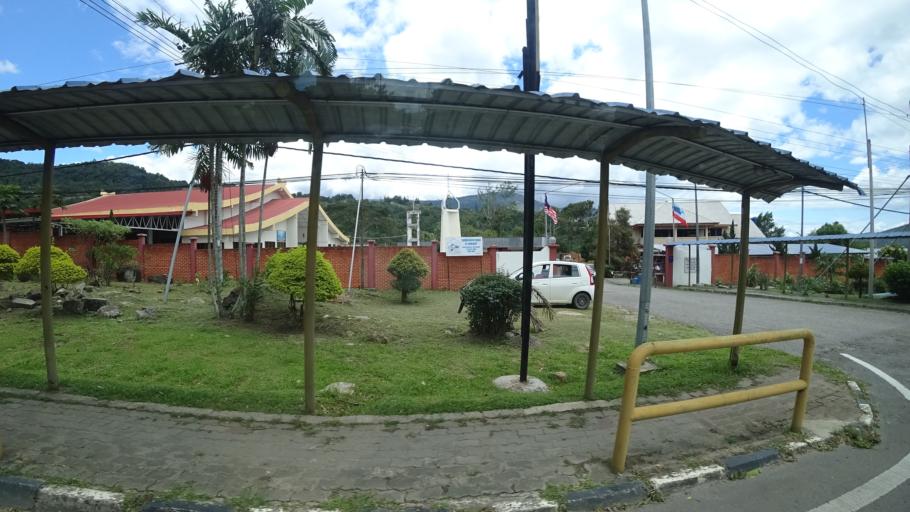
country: MY
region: Sabah
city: Ranau
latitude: 5.9544
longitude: 116.6638
